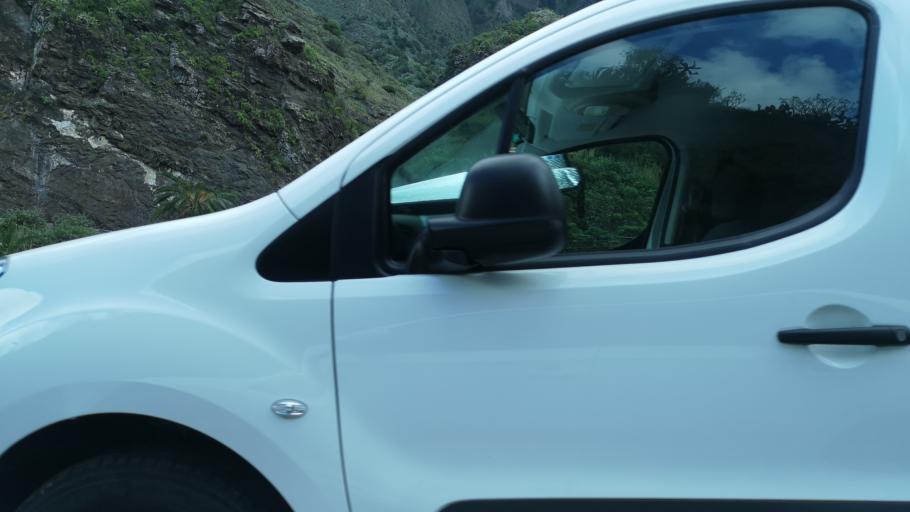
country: ES
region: Canary Islands
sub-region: Provincia de Santa Cruz de Tenerife
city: Hermigua
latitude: 28.1423
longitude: -17.1948
